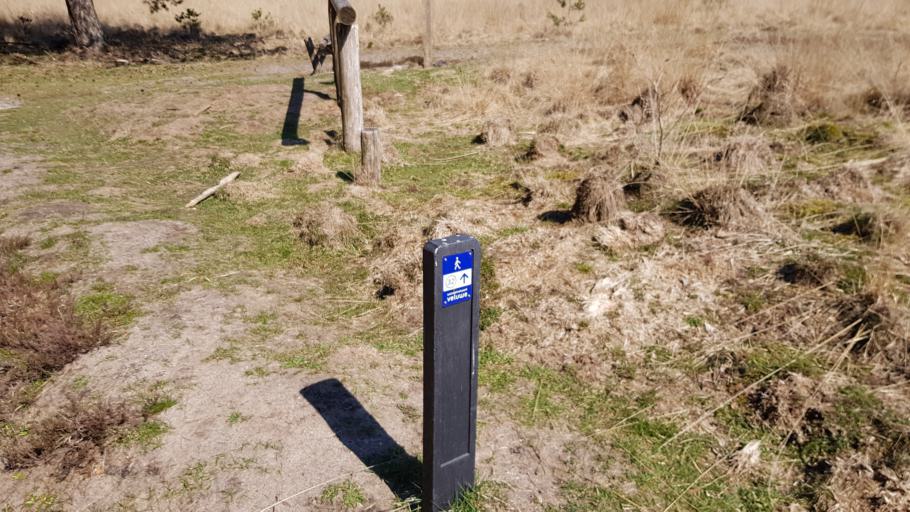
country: NL
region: Gelderland
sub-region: Gemeente Rheden
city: Rheden
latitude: 52.0576
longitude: 6.0047
